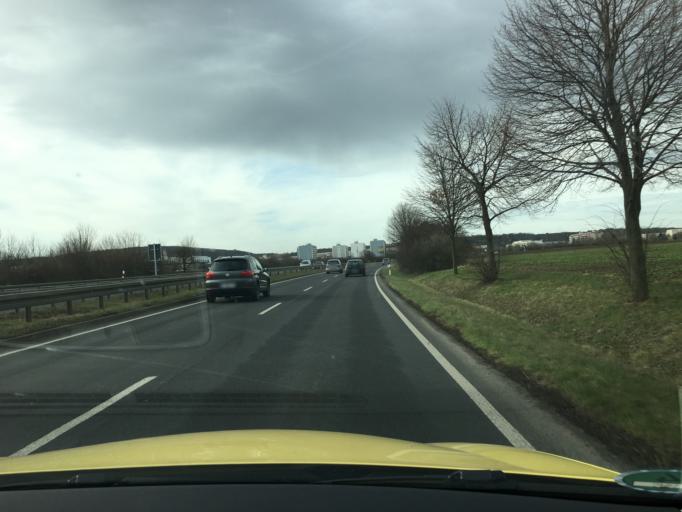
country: DE
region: Thuringia
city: Erfurt
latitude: 50.9608
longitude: 11.0878
